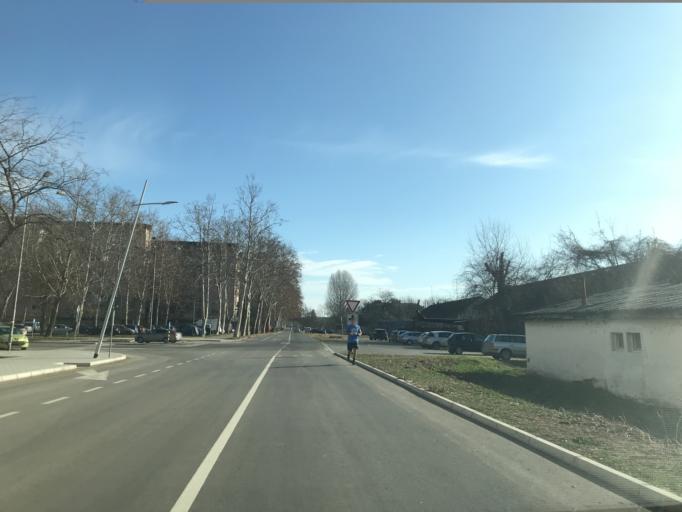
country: RS
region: Autonomna Pokrajina Vojvodina
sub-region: Juznobacki Okrug
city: Novi Sad
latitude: 45.2355
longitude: 19.8334
